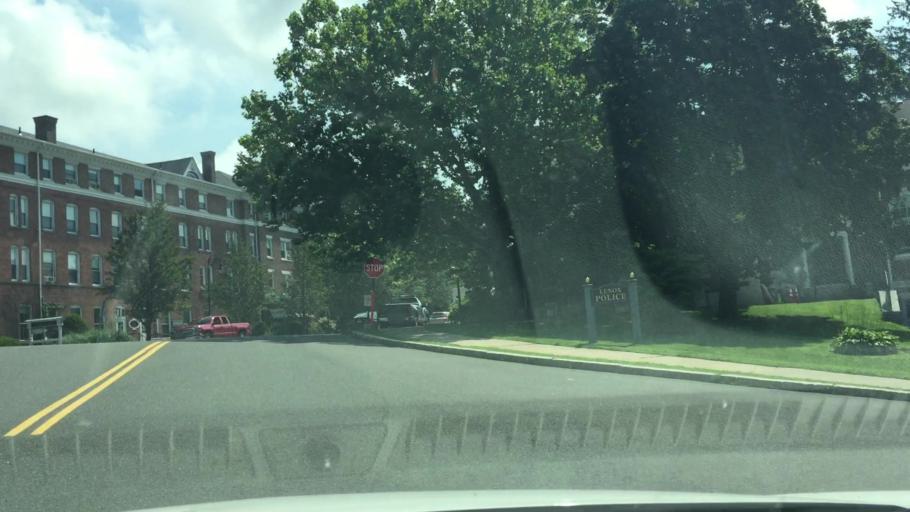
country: US
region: Massachusetts
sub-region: Berkshire County
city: Lenox
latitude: 42.3568
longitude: -73.2852
